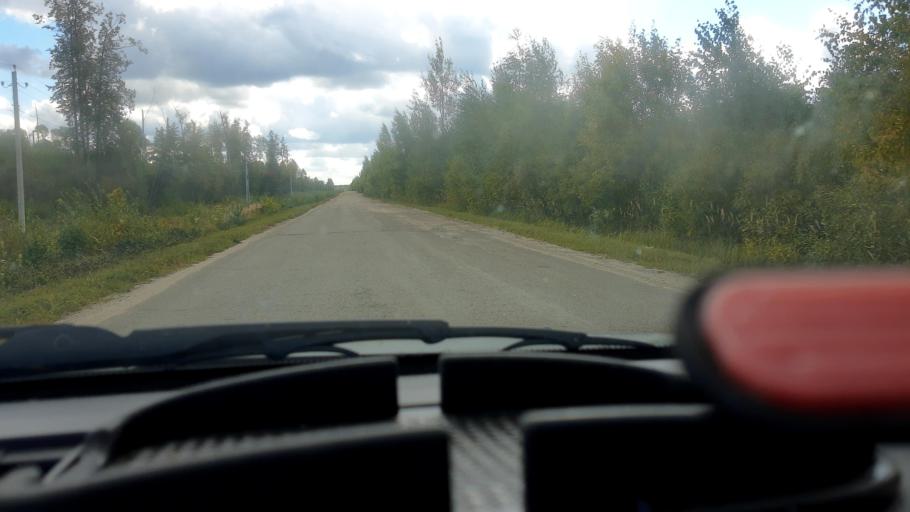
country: RU
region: Mariy-El
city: Kilemary
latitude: 56.8969
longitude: 46.7478
